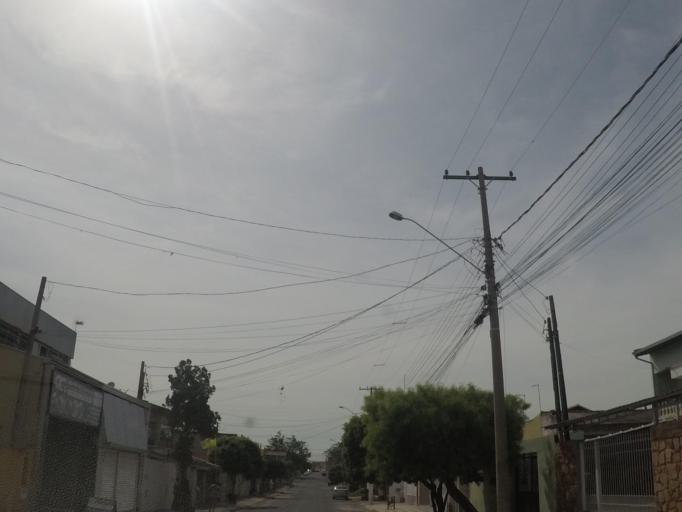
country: BR
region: Sao Paulo
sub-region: Hortolandia
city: Hortolandia
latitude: -22.8477
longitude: -47.1944
